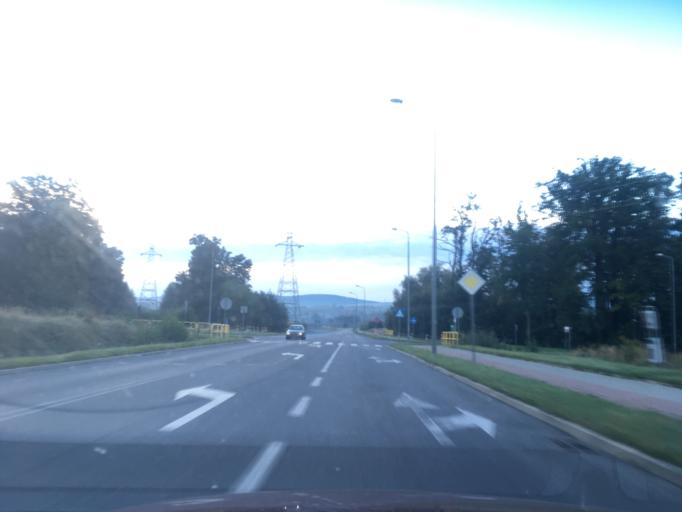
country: PL
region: Lower Silesian Voivodeship
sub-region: Powiat zgorzelecki
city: Bogatynia
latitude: 50.9160
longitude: 14.9584
